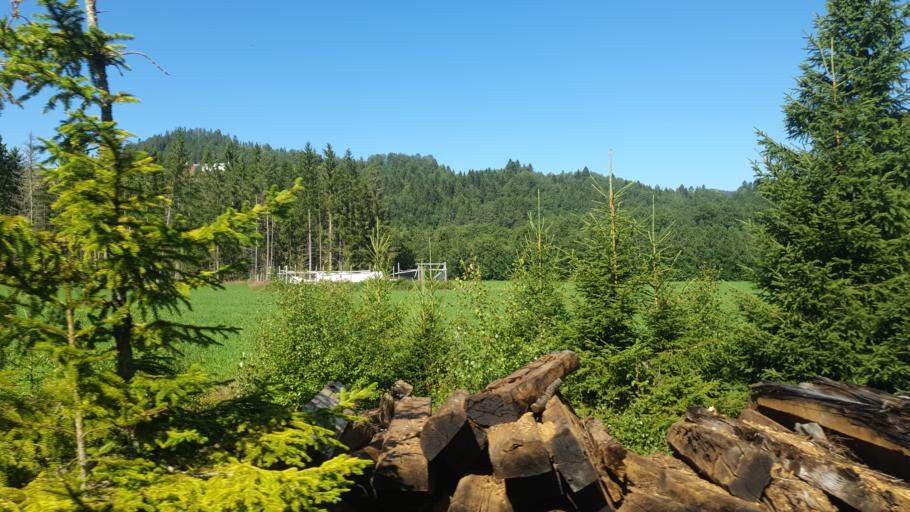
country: NO
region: Sor-Trondelag
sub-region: Meldal
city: Meldal
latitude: 63.1799
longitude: 9.7638
